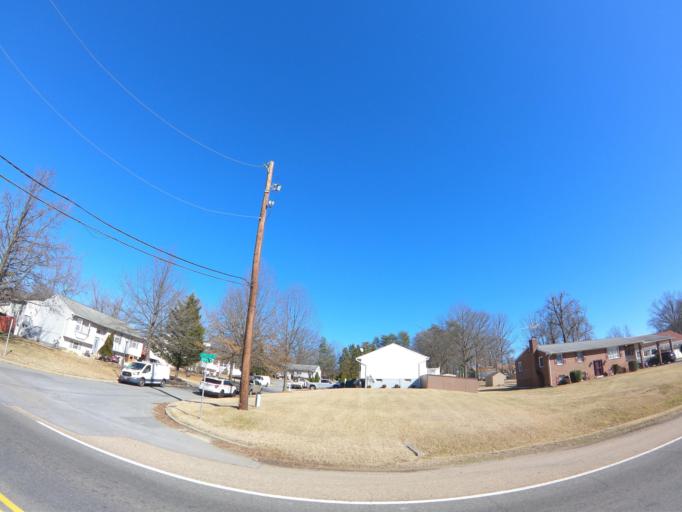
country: US
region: Maryland
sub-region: Prince George's County
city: Beltsville
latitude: 39.0395
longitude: -76.8984
